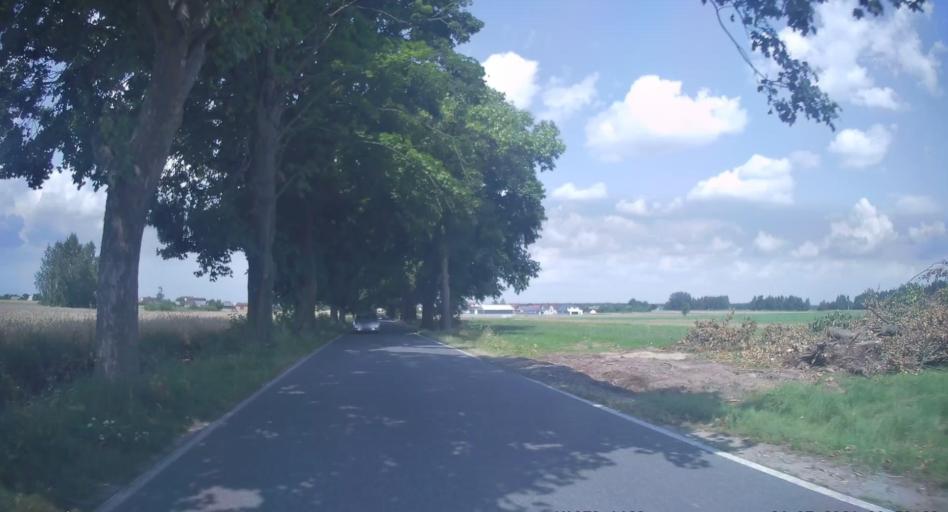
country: PL
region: Lodz Voivodeship
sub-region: Powiat tomaszowski
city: Lubochnia
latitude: 51.5641
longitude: 20.1196
